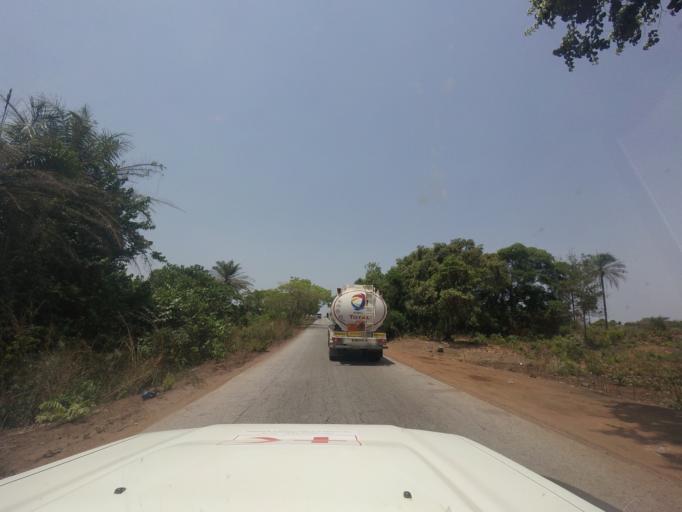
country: GN
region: Kindia
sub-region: Coyah
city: Coyah
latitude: 9.8353
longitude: -13.1393
